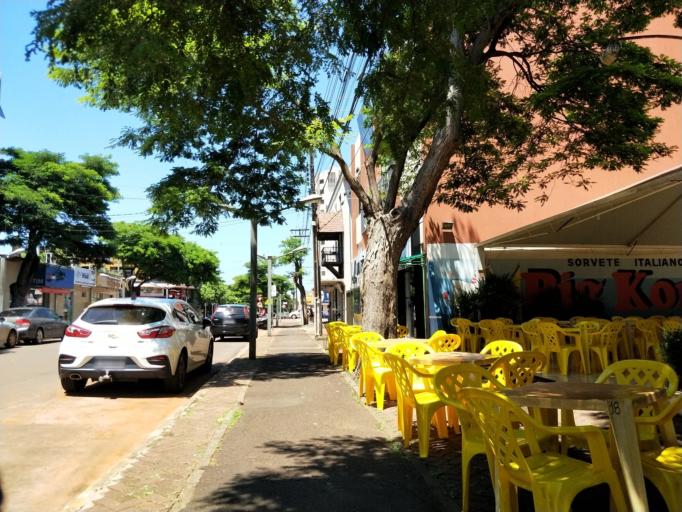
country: BR
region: Parana
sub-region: Marechal Candido Rondon
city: Marechal Candido Rondon
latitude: -24.5627
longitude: -54.0613
